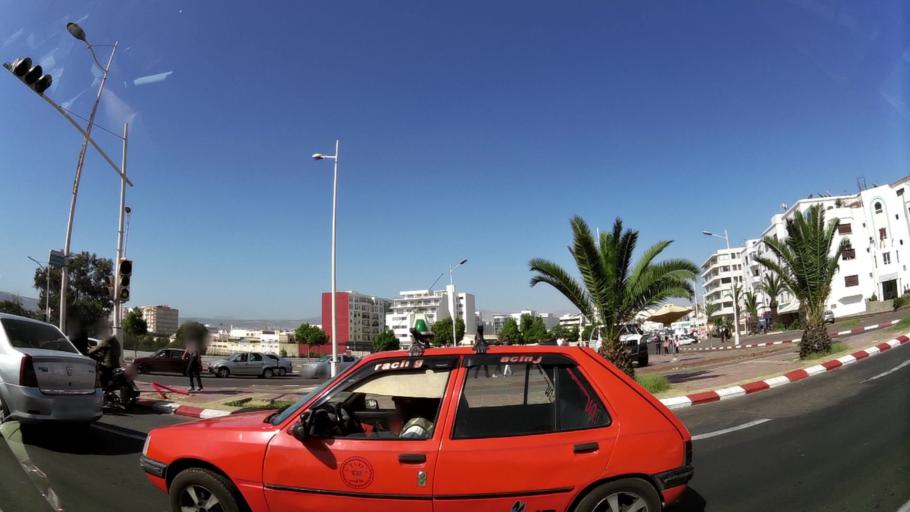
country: MA
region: Souss-Massa-Draa
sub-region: Agadir-Ida-ou-Tnan
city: Agadir
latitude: 30.4107
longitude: -9.5928
